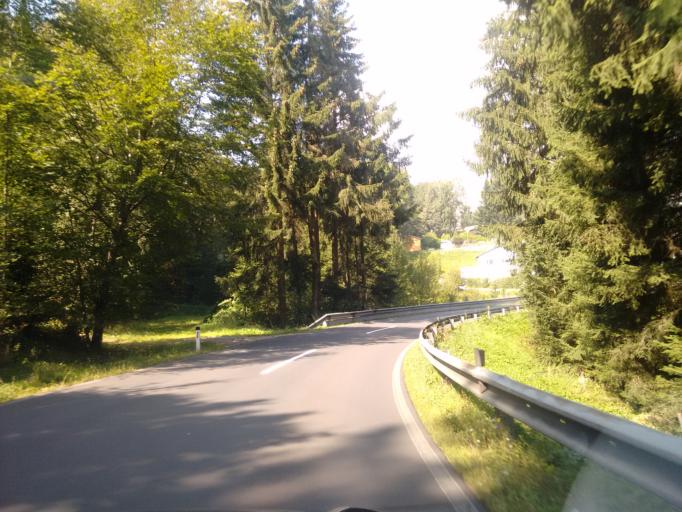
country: AT
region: Upper Austria
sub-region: Politischer Bezirk Urfahr-Umgebung
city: Altenberg bei Linz
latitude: 48.3922
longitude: 14.3408
